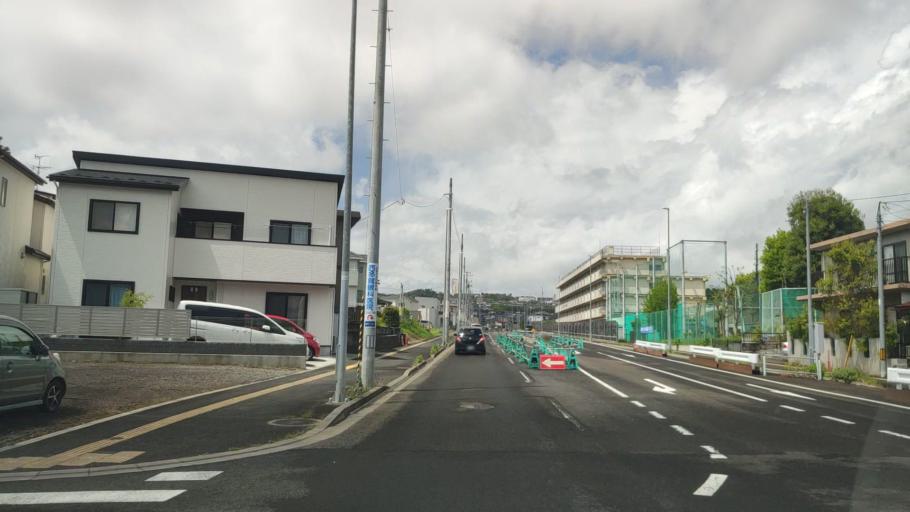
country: JP
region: Miyagi
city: Sendai
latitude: 38.2293
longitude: 140.8572
